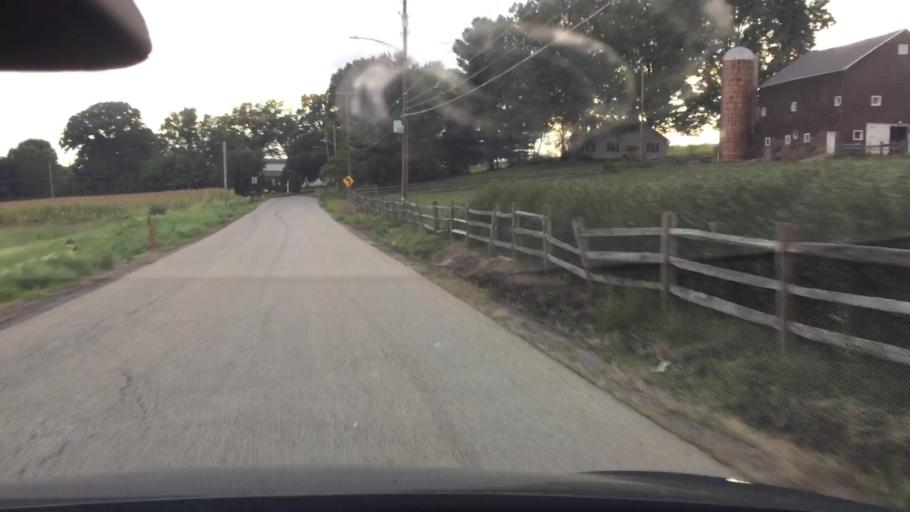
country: US
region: Pennsylvania
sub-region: Butler County
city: Meadowood
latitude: 40.8369
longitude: -79.8779
